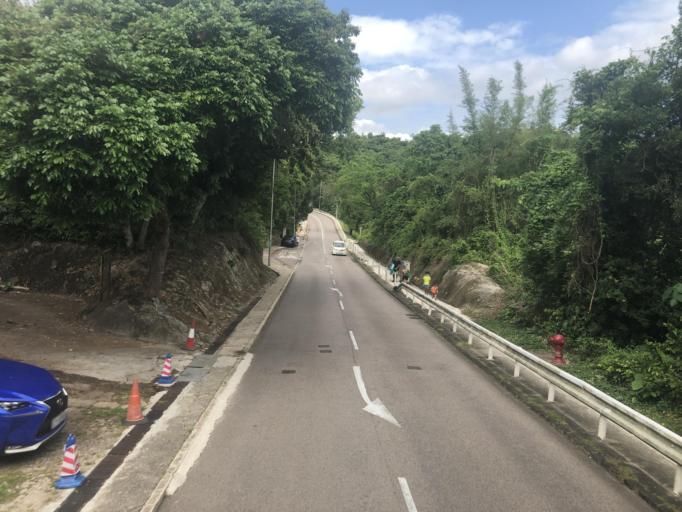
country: HK
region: Sai Kung
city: Sai Kung
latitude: 22.3941
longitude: 114.3153
